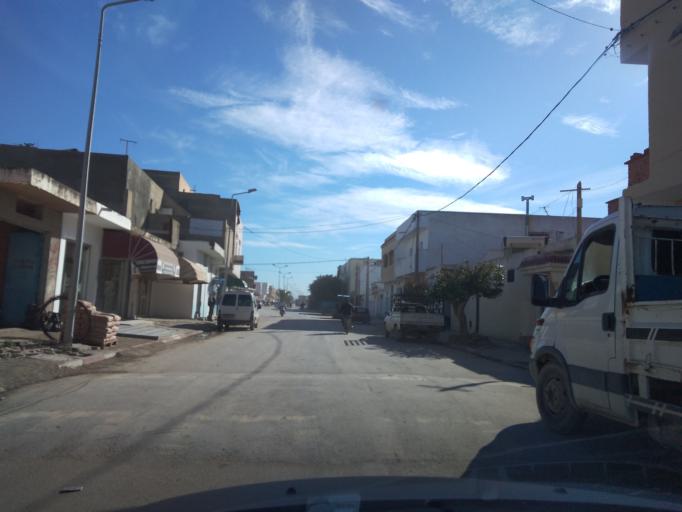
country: TN
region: Ariana
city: Qal'at al Andalus
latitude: 37.0612
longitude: 10.1187
